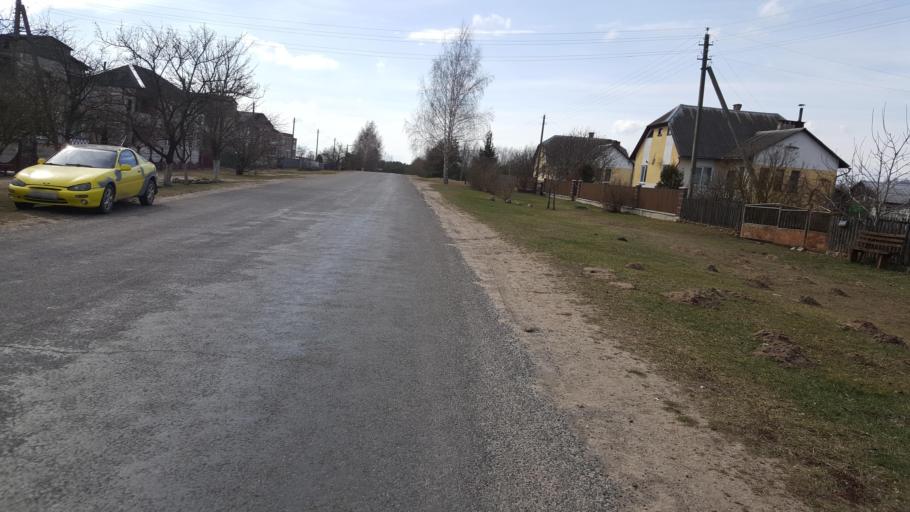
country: BY
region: Brest
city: Kamyanyets
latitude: 52.3942
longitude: 23.9977
